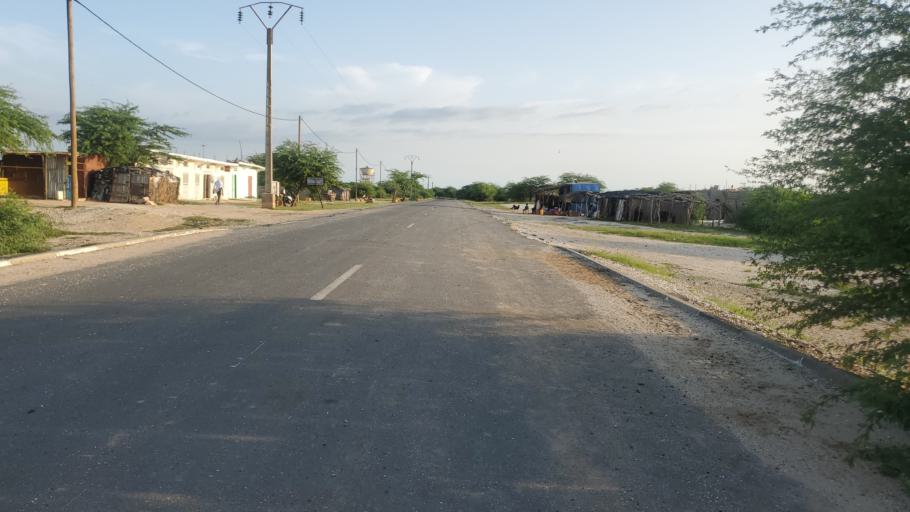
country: SN
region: Saint-Louis
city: Saint-Louis
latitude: 16.2126
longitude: -16.4153
